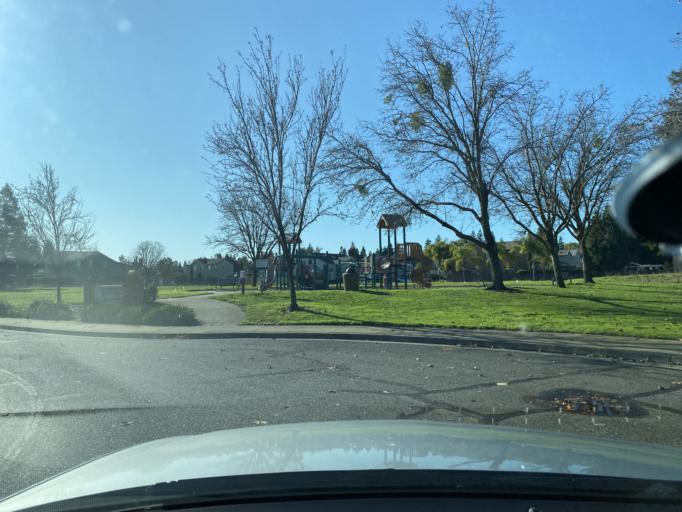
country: US
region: California
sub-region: Sacramento County
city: Elk Grove
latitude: 38.4346
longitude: -121.3852
